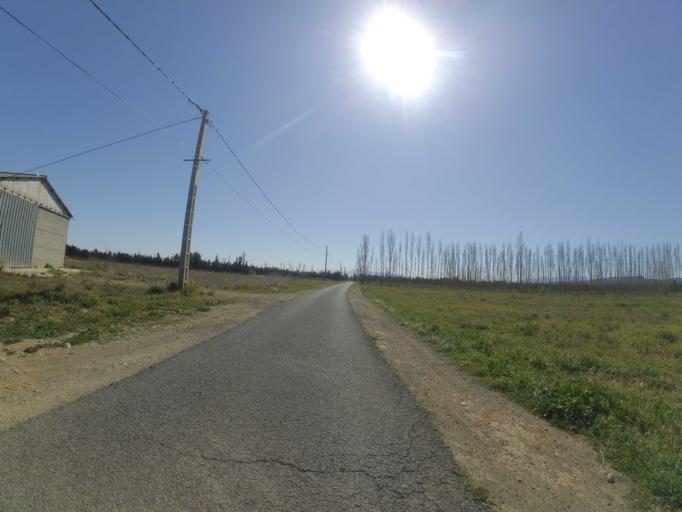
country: FR
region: Languedoc-Roussillon
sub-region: Departement des Pyrenees-Orientales
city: Corneilla-la-Riviere
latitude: 42.6799
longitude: 2.7226
